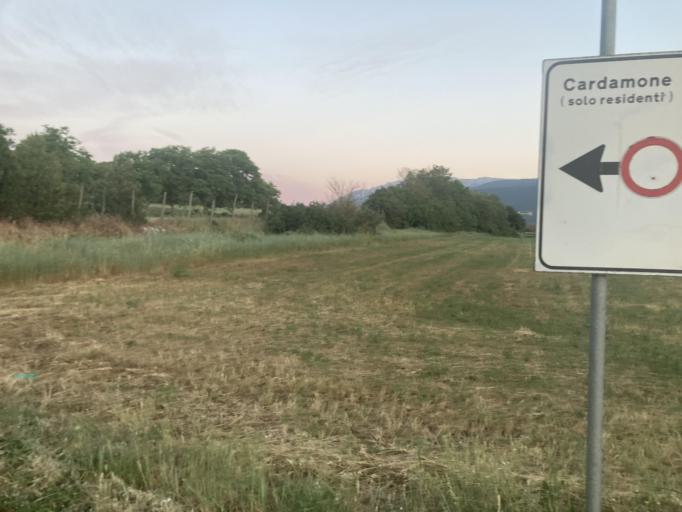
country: IT
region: Abruzzo
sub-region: Provincia dell' Aquila
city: San Demetrio Ne' Vestini
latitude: 42.2947
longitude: 13.5535
